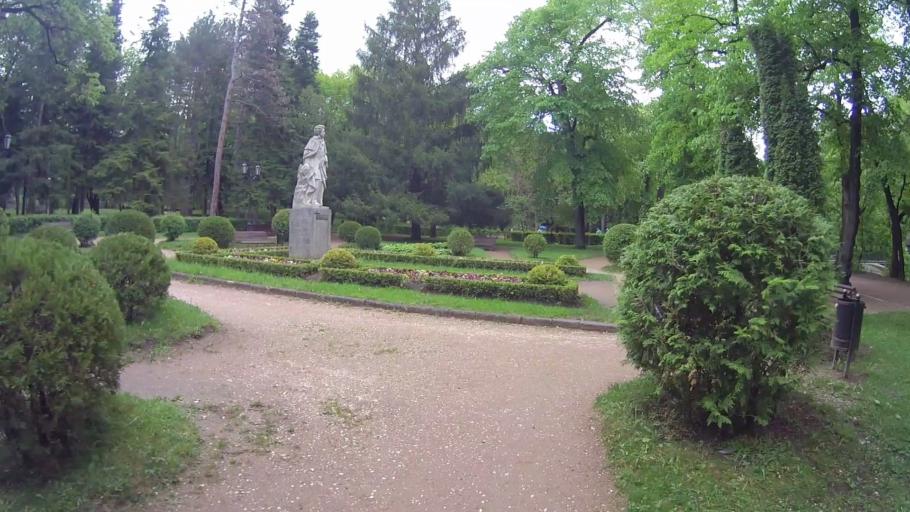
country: RU
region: Stavropol'skiy
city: Kislovodsk
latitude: 43.8955
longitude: 42.7190
